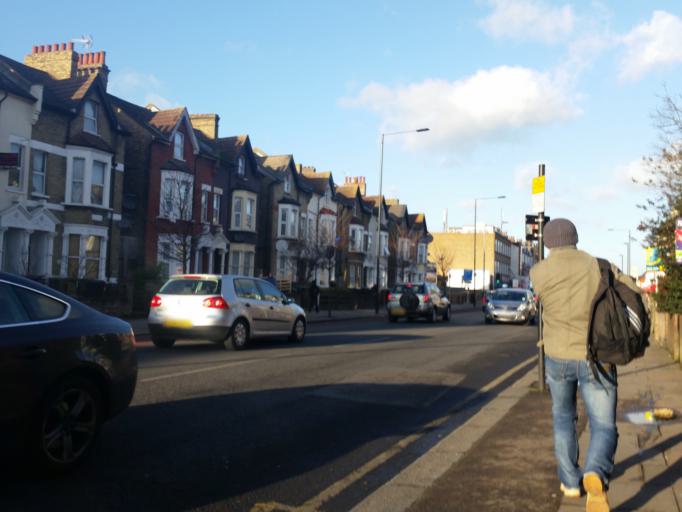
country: GB
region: England
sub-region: Greater London
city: Wood Green
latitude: 51.6073
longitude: -0.1108
